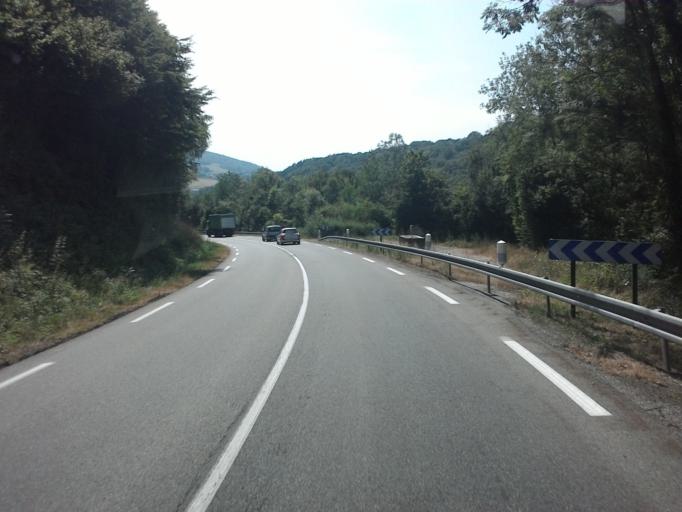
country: FR
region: Rhone-Alpes
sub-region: Departement de l'Isere
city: Bilieu
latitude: 45.4552
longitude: 5.5699
